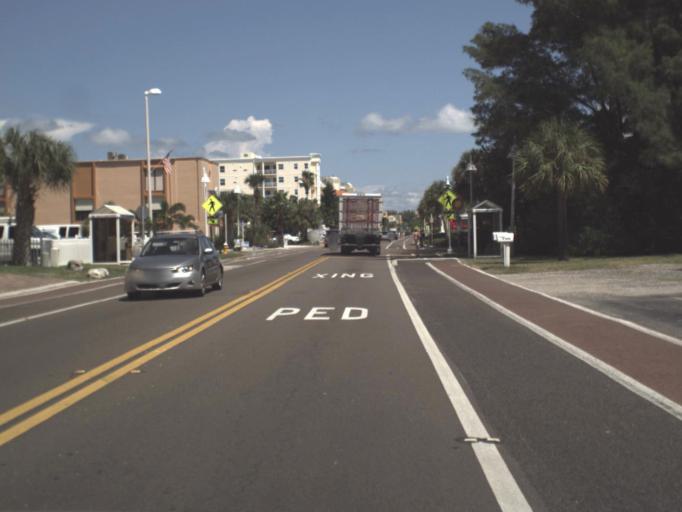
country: US
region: Florida
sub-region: Pinellas County
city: Indian Shores
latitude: 27.8468
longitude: -82.8427
